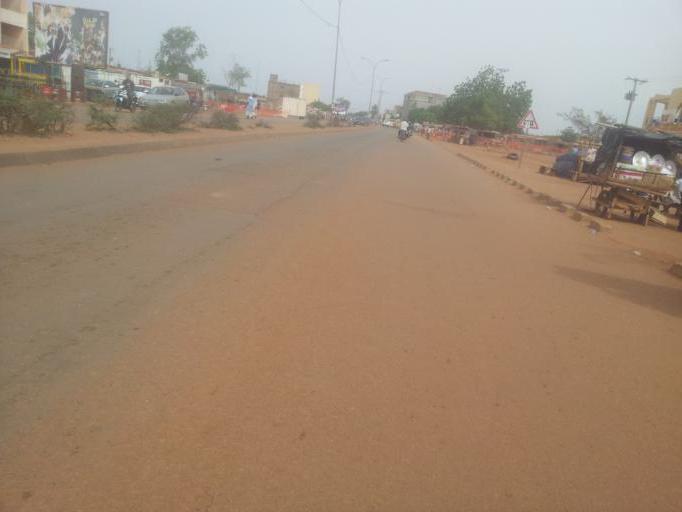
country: BF
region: Centre
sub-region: Kadiogo Province
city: Ouagadougou
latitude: 12.3871
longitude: -1.5625
